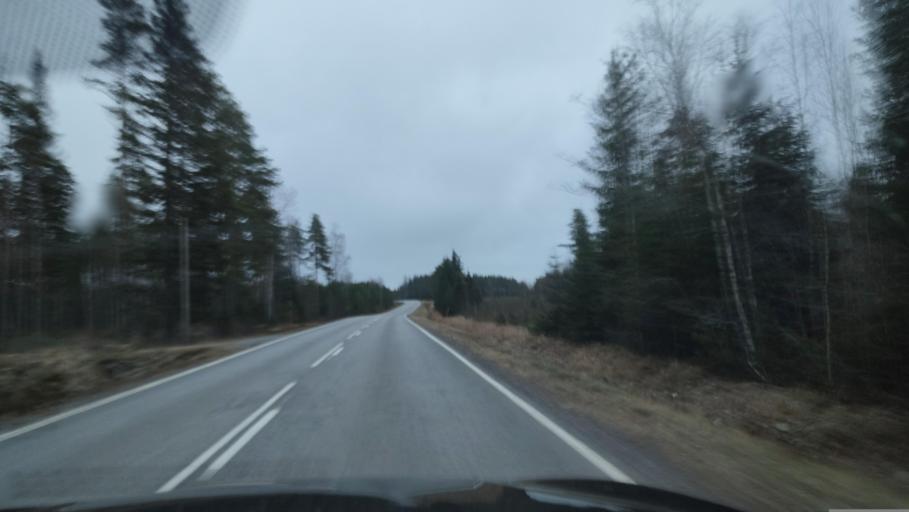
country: FI
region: Southern Ostrobothnia
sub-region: Suupohja
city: Karijoki
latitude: 62.3318
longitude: 21.9073
